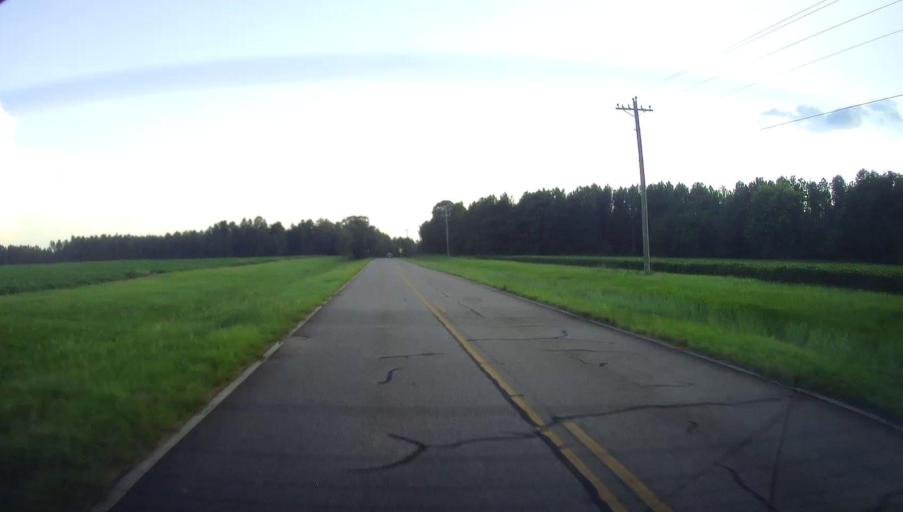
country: US
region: Georgia
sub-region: Peach County
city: Fort Valley
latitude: 32.6013
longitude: -83.8358
